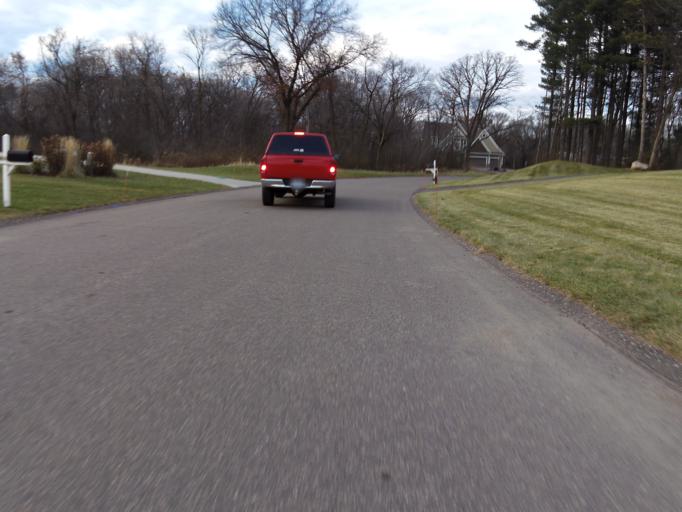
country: US
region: Minnesota
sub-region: Washington County
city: Bayport
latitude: 45.0036
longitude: -92.8003
